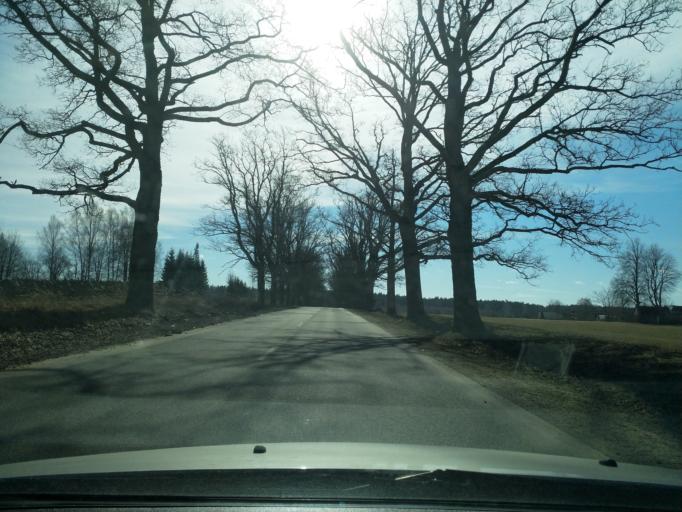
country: LV
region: Valmieras Rajons
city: Valmiera
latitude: 57.5164
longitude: 25.4208
